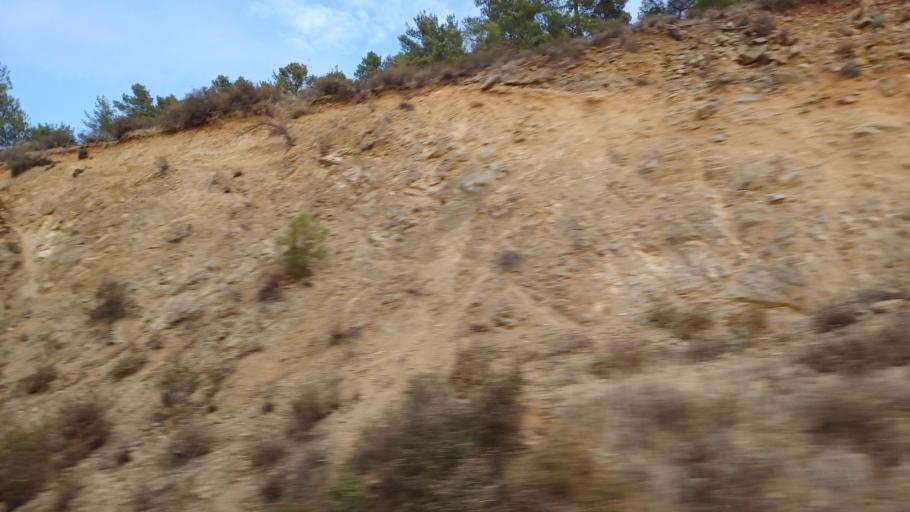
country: CY
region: Lefkosia
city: Kakopetria
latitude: 34.9803
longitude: 32.9085
